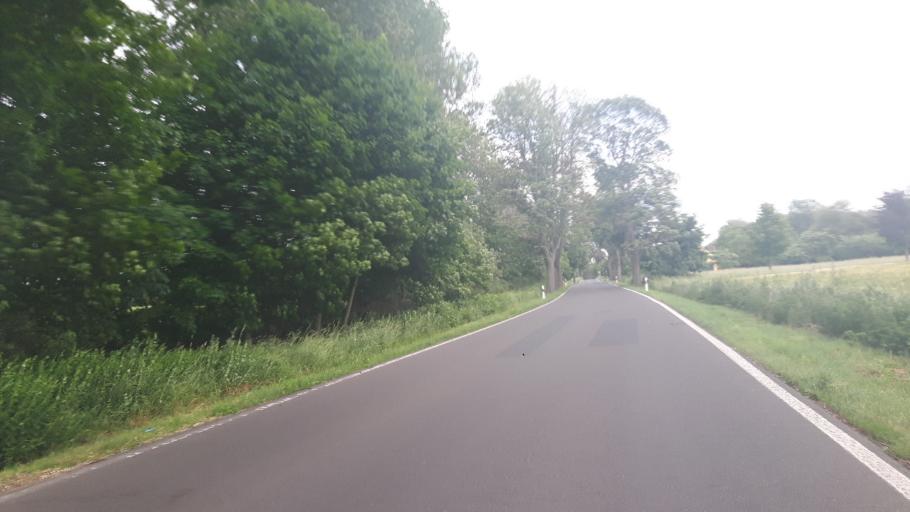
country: DE
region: Brandenburg
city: Hohenfinow
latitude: 52.7720
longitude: 13.8617
